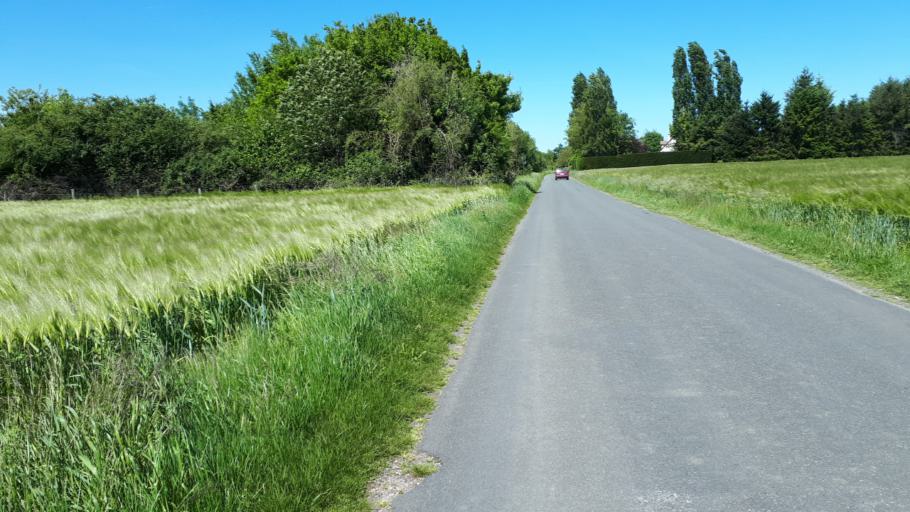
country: FR
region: Centre
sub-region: Departement du Loir-et-Cher
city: Villiers-sur-Loir
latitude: 47.7889
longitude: 1.0012
